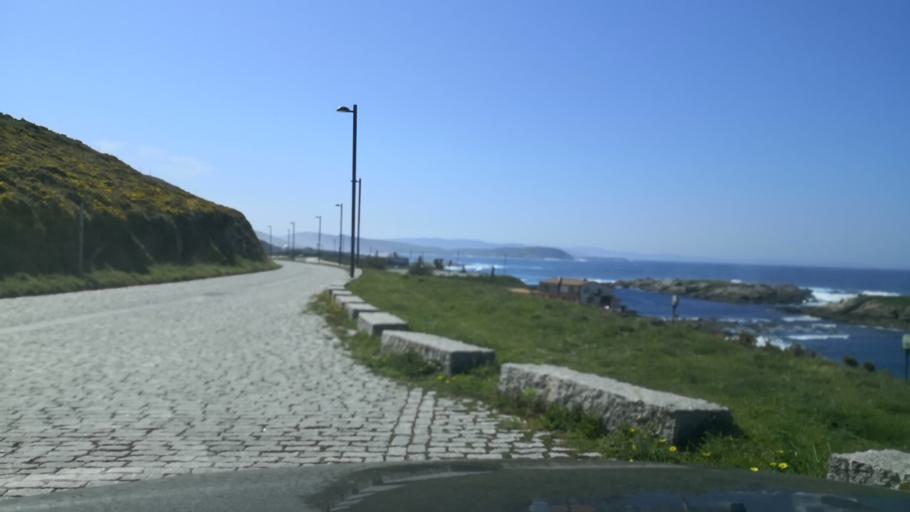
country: ES
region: Galicia
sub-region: Provincia da Coruna
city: A Coruna
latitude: 43.3789
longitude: -8.4432
